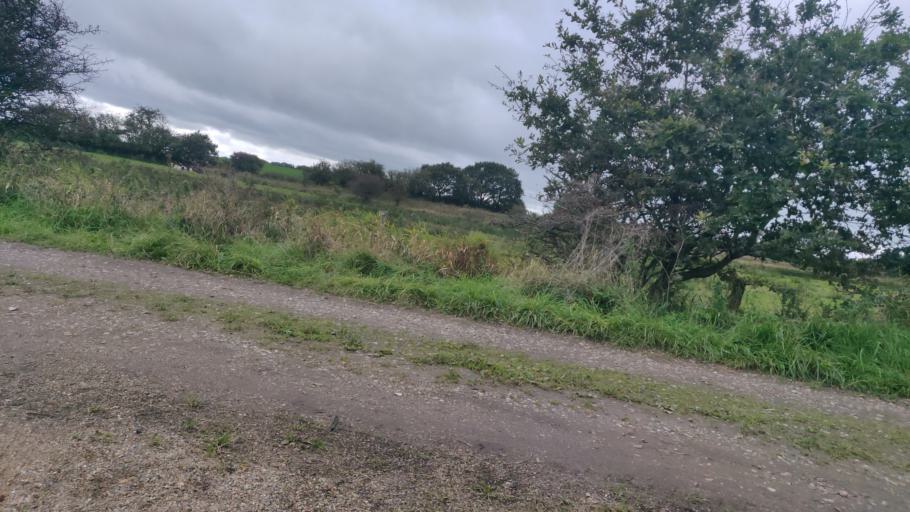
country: DK
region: South Denmark
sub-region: Kolding Kommune
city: Lunderskov
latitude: 55.5384
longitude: 9.3383
